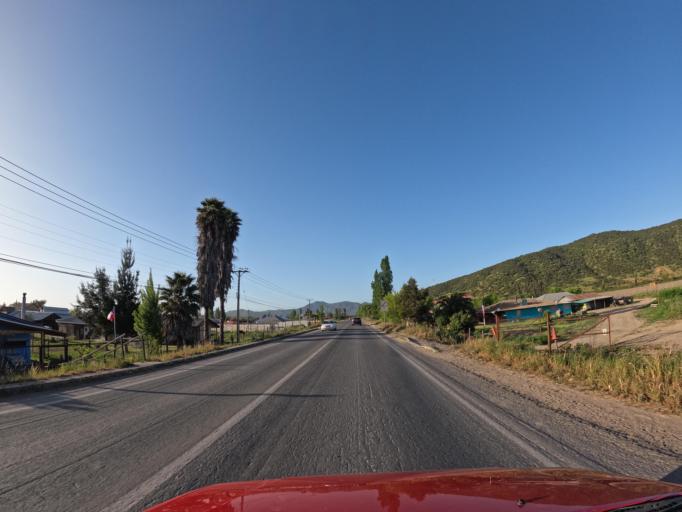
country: CL
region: O'Higgins
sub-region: Provincia de Colchagua
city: Santa Cruz
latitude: -34.4127
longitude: -71.3726
